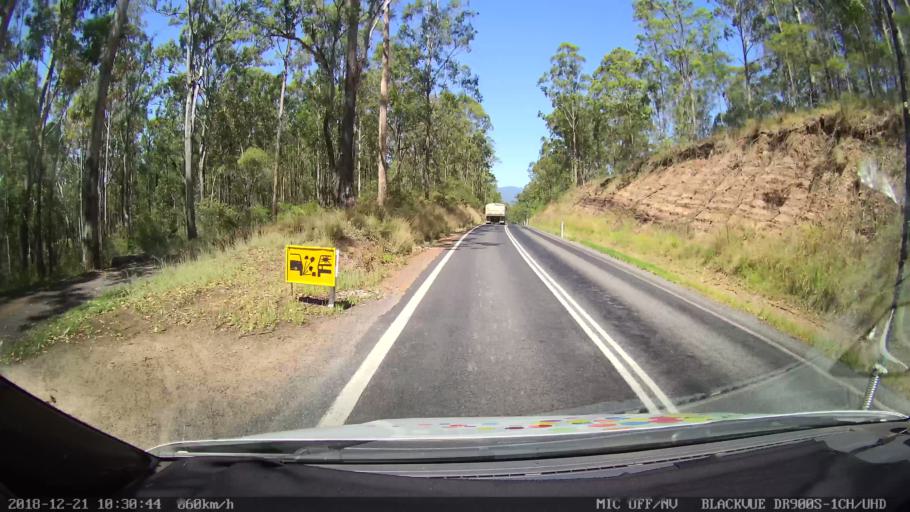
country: AU
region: New South Wales
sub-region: Clarence Valley
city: South Grafton
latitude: -29.6330
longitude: 152.7050
